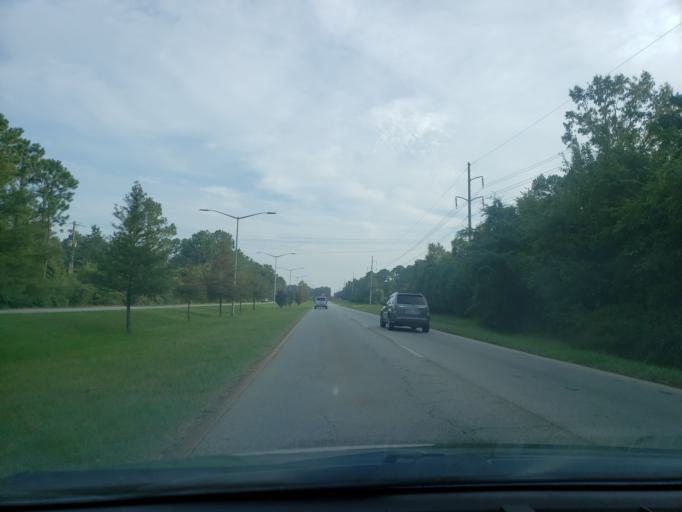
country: US
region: Georgia
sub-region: Dougherty County
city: Albany
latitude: 31.5945
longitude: -84.2194
